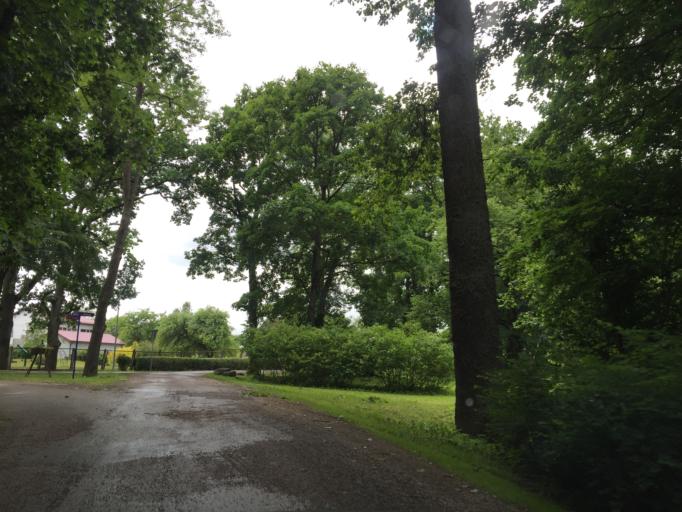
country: LV
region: Lecava
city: Iecava
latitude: 56.5933
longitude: 24.2023
